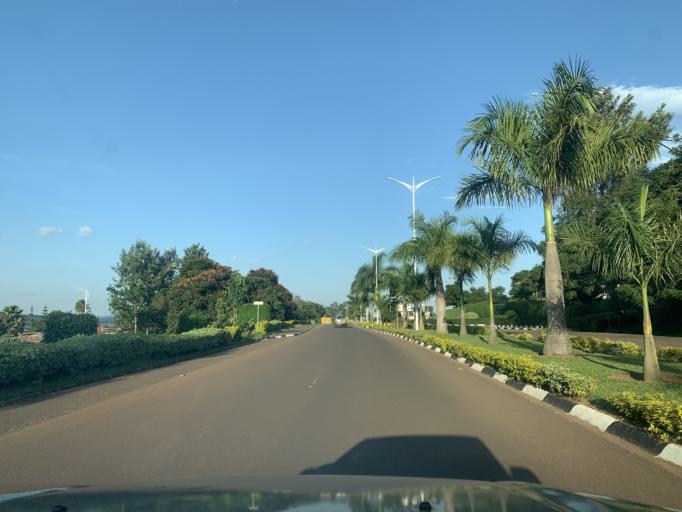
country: RW
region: Kigali
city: Kigali
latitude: -1.9634
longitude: 30.1326
